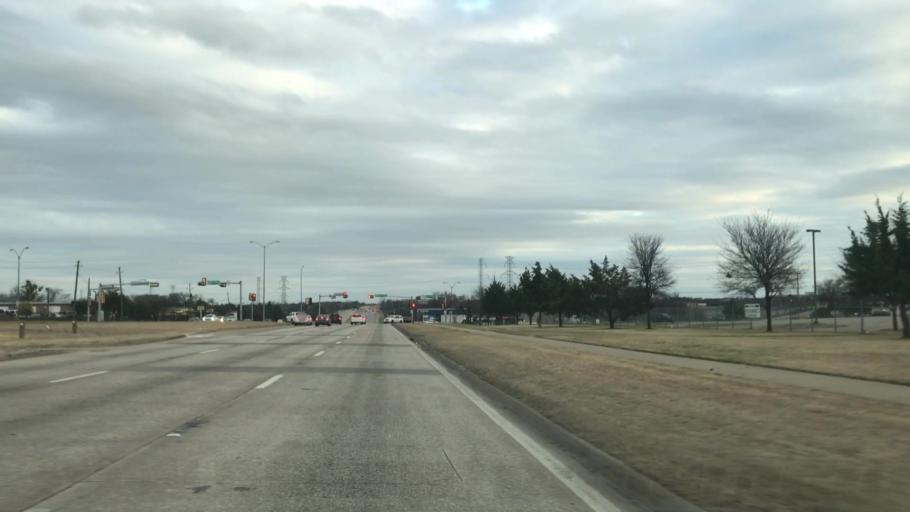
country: US
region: Texas
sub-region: Dallas County
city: Cockrell Hill
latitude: 32.7123
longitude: -96.9098
